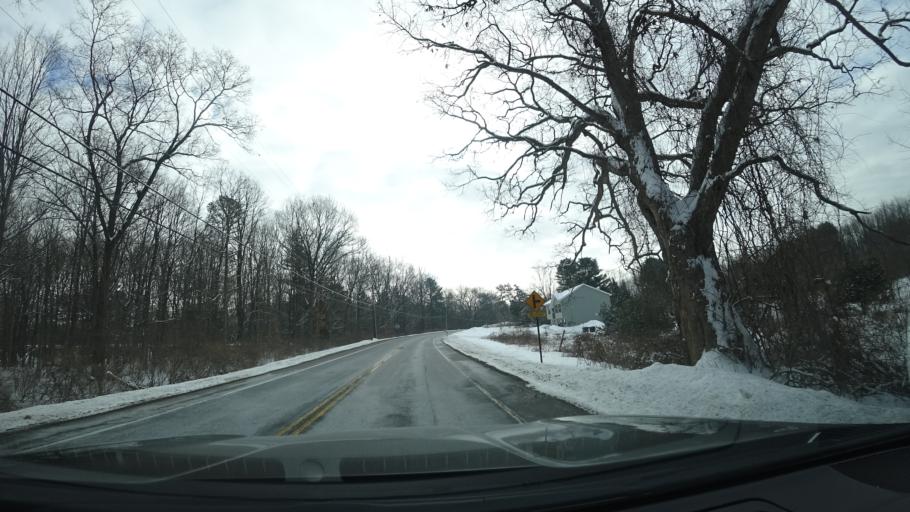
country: US
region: New York
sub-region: Saratoga County
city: South Glens Falls
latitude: 43.2840
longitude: -73.6202
